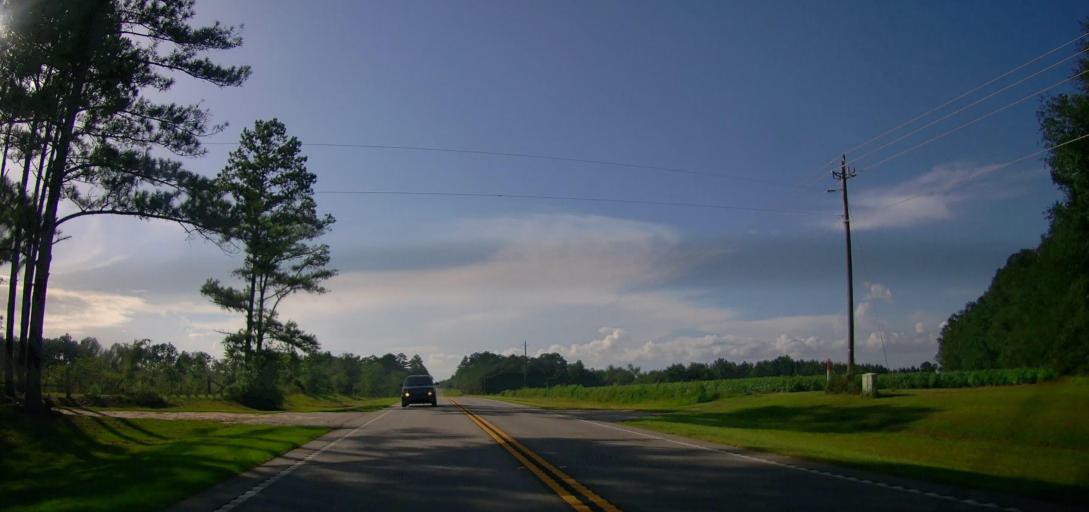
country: US
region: Georgia
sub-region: Coffee County
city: Nicholls
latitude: 31.3974
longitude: -82.6677
